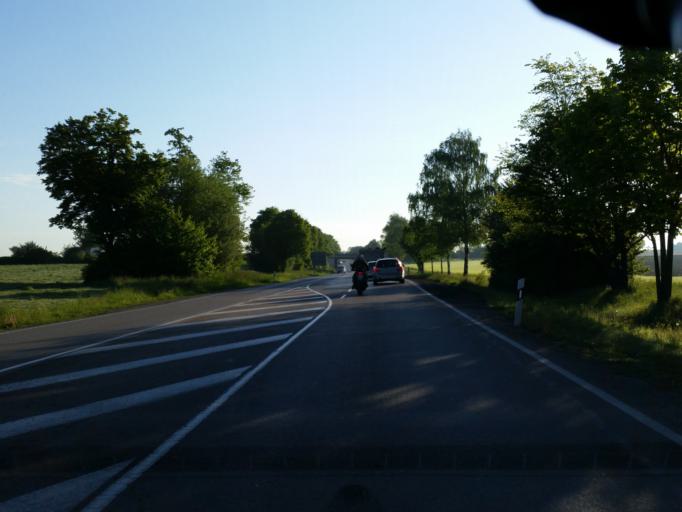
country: DE
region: Bavaria
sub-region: Upper Bavaria
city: Landsberg am Lech
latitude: 48.0553
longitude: 10.9046
